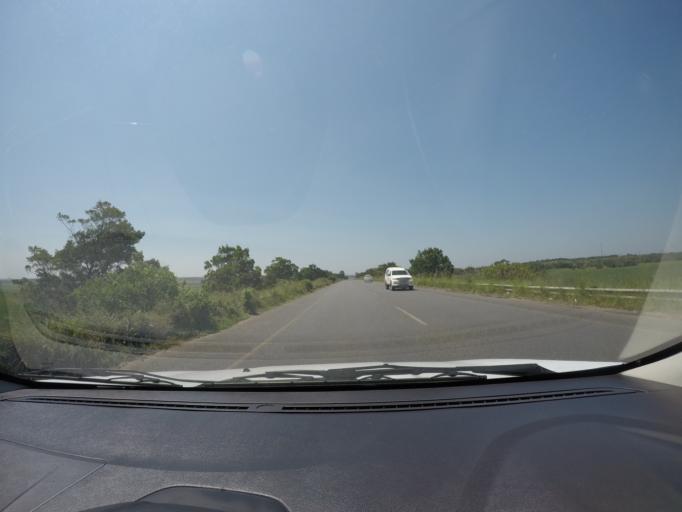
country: ZA
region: KwaZulu-Natal
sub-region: uThungulu District Municipality
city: Empangeni
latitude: -28.7829
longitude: 31.9580
